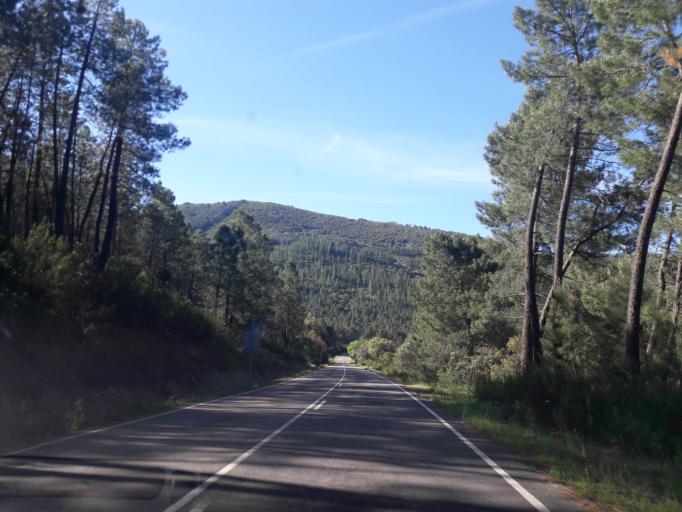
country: ES
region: Castille and Leon
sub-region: Provincia de Salamanca
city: Sotoserrano
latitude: 40.4109
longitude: -6.0531
